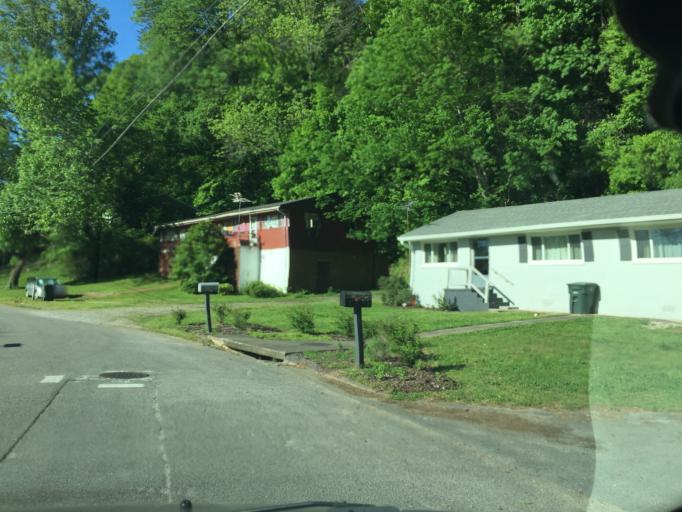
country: US
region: Tennessee
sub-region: Hamilton County
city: Lookout Mountain
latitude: 34.9928
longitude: -85.3329
